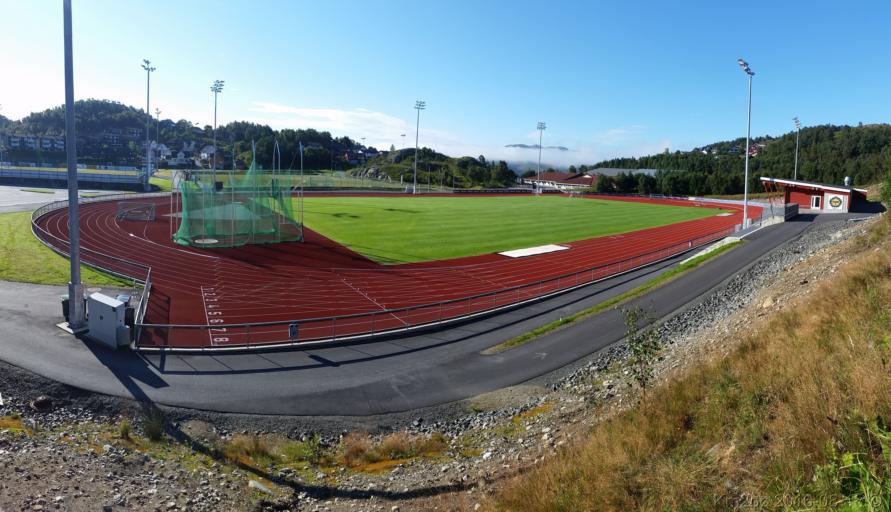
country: NO
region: Rogaland
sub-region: Gjesdal
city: Algard
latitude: 58.7758
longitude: 5.8644
